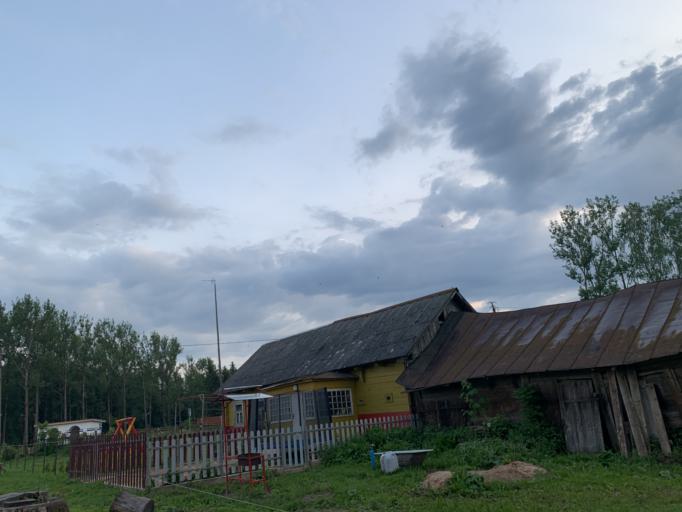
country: BY
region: Minsk
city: Tsimkavichy
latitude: 53.1262
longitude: 26.8827
